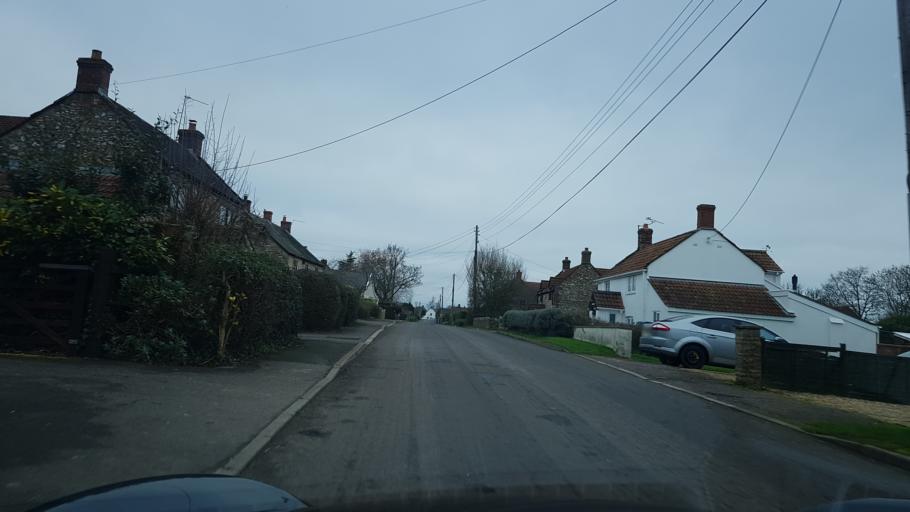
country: GB
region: England
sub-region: Somerset
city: Chard
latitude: 50.9259
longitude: -2.9648
